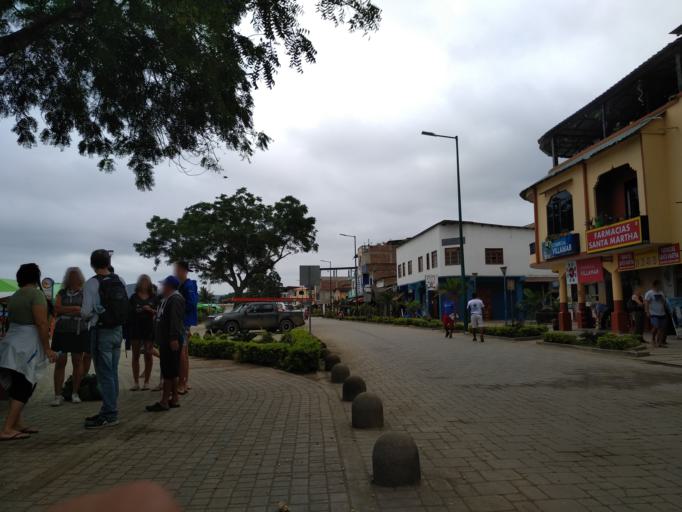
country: EC
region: Manabi
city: Jipijapa
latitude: -1.5597
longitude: -80.8135
